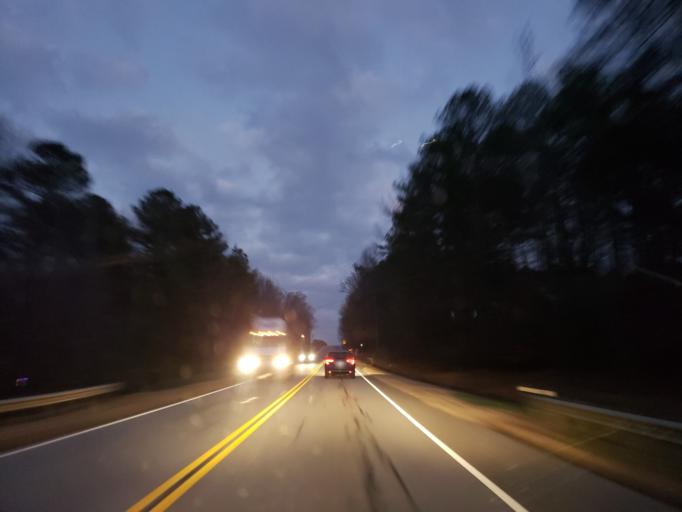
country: US
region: Georgia
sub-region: Carroll County
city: Temple
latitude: 33.8369
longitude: -85.0063
